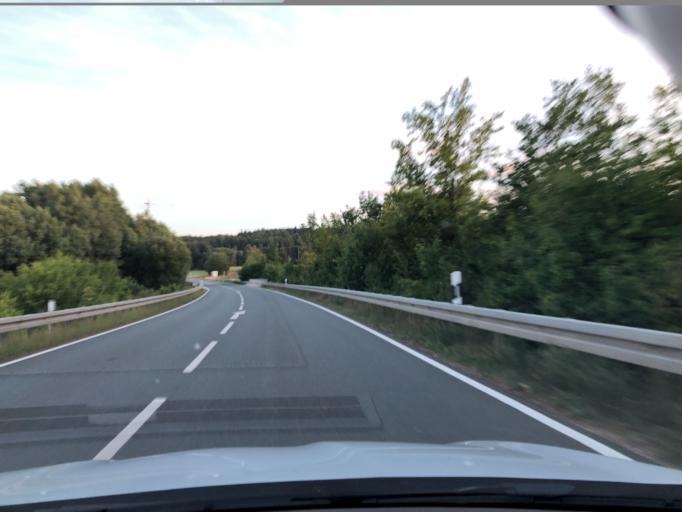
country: DE
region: Bavaria
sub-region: Upper Palatinate
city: Illschwang
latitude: 49.4457
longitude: 11.6594
